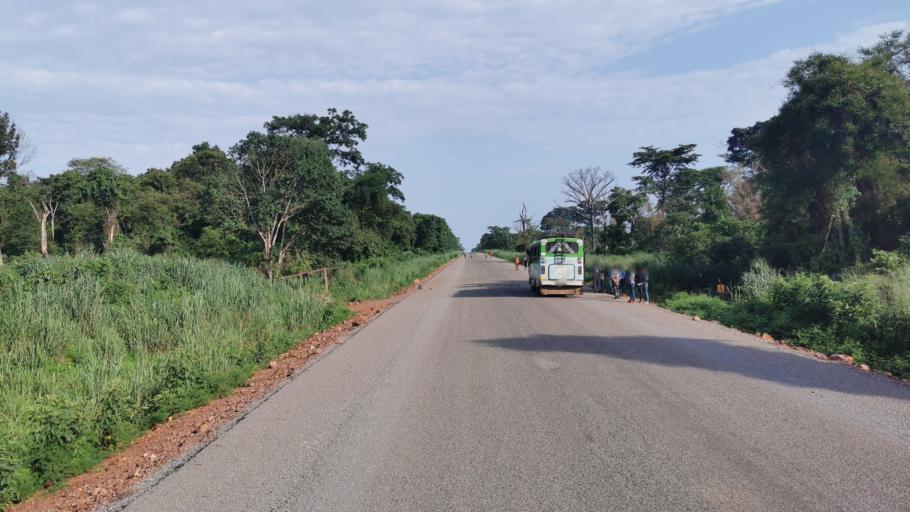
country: ET
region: Gambela
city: Gambela
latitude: 7.7074
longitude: 34.6633
